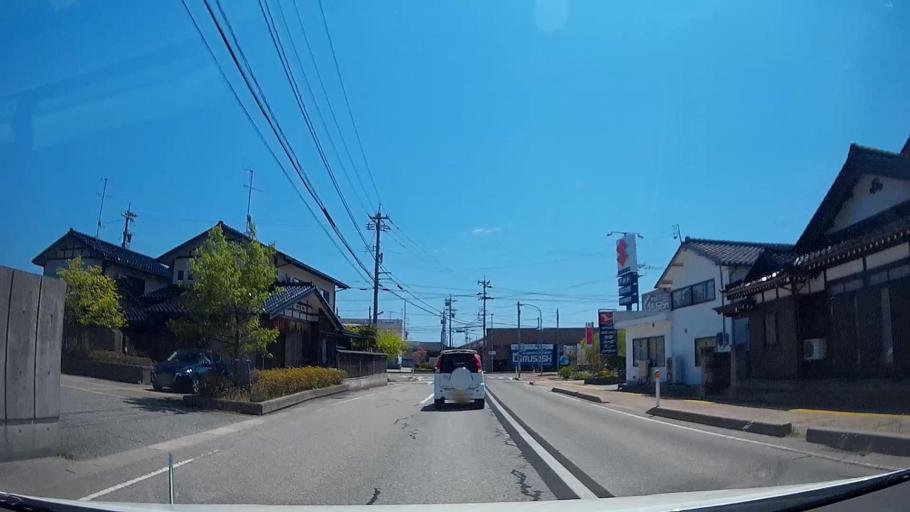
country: JP
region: Ishikawa
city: Nanao
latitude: 37.4419
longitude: 137.2729
